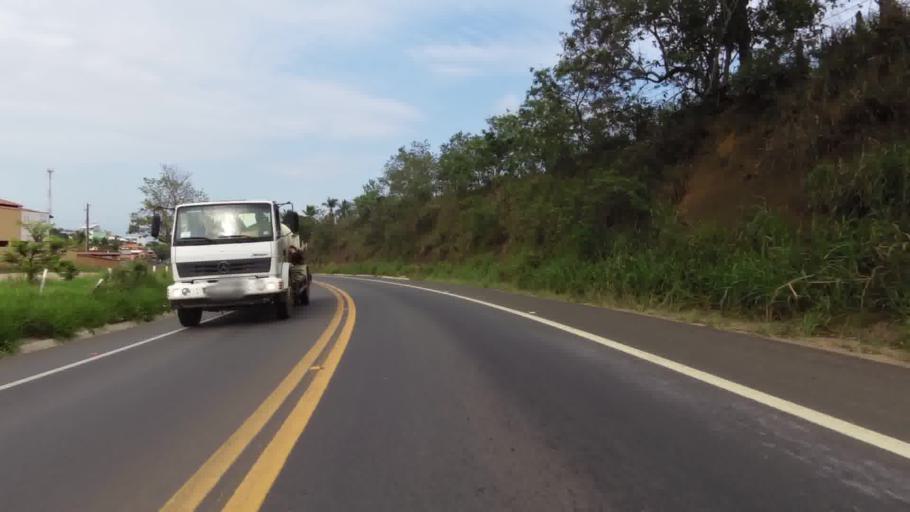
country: BR
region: Espirito Santo
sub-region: Piuma
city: Piuma
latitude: -20.8226
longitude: -40.6964
